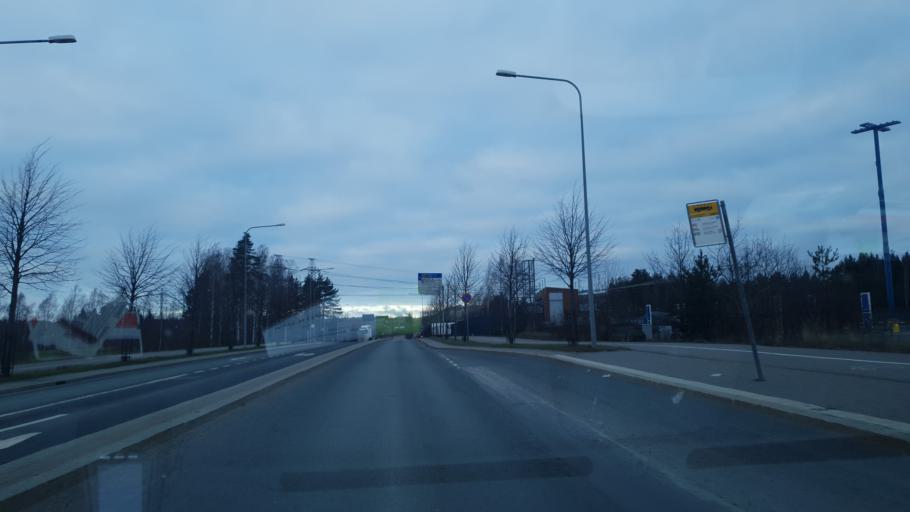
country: FI
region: Uusimaa
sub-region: Helsinki
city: Vantaa
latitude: 60.2165
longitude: 25.1649
